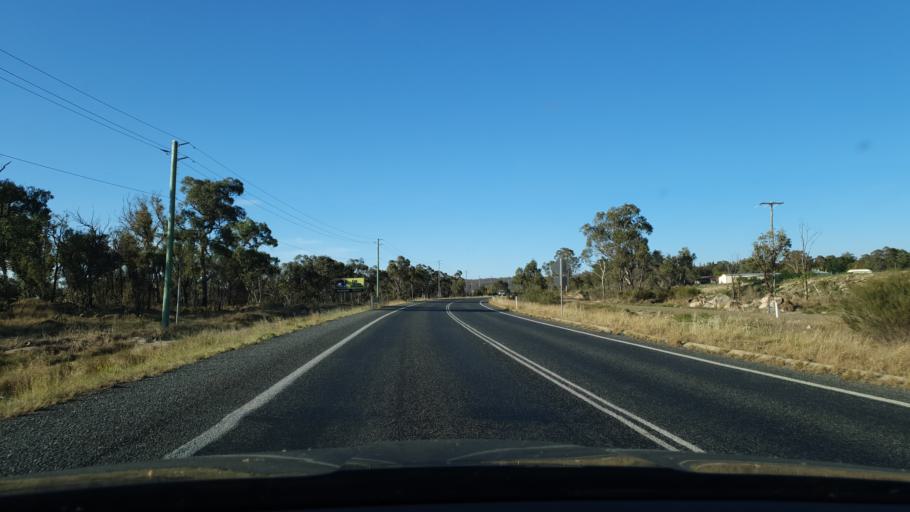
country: AU
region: Queensland
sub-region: Southern Downs
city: Stanthorpe
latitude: -28.6664
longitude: 151.9154
